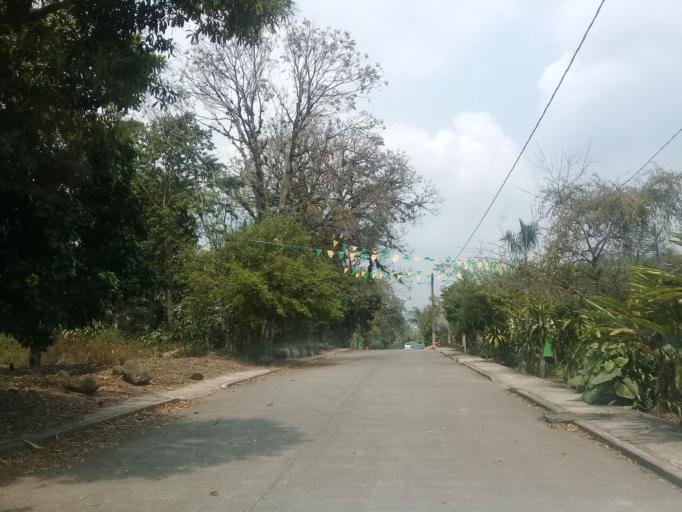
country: MX
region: Veracruz
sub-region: Cordoba
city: San Jose de Tapia
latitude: 18.8263
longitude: -96.9792
